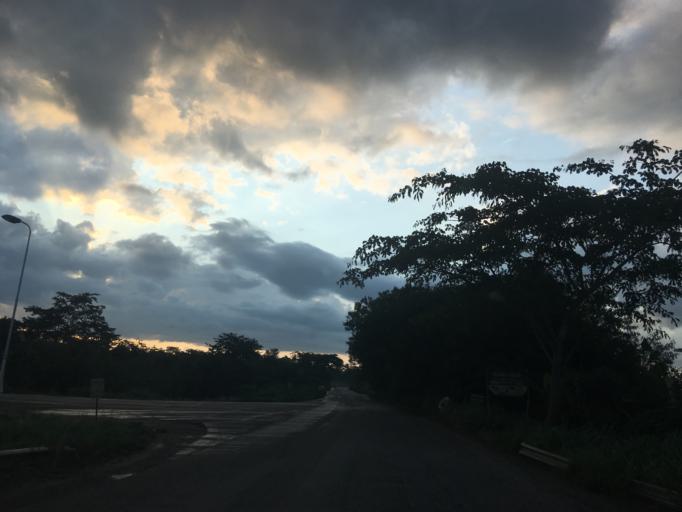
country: GH
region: Western
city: Bibiani
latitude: 6.7636
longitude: -2.5057
